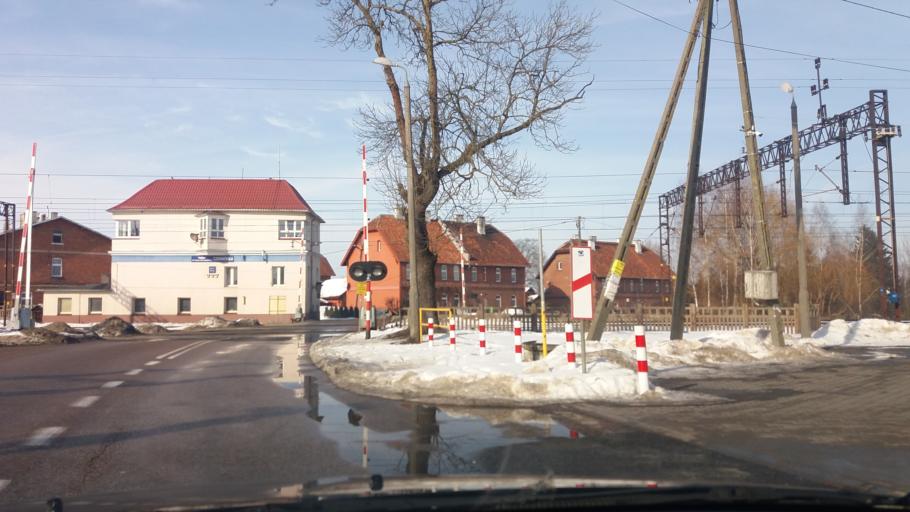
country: PL
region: Warmian-Masurian Voivodeship
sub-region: Powiat olsztynski
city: Czerwonka
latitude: 53.9157
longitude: 20.8973
